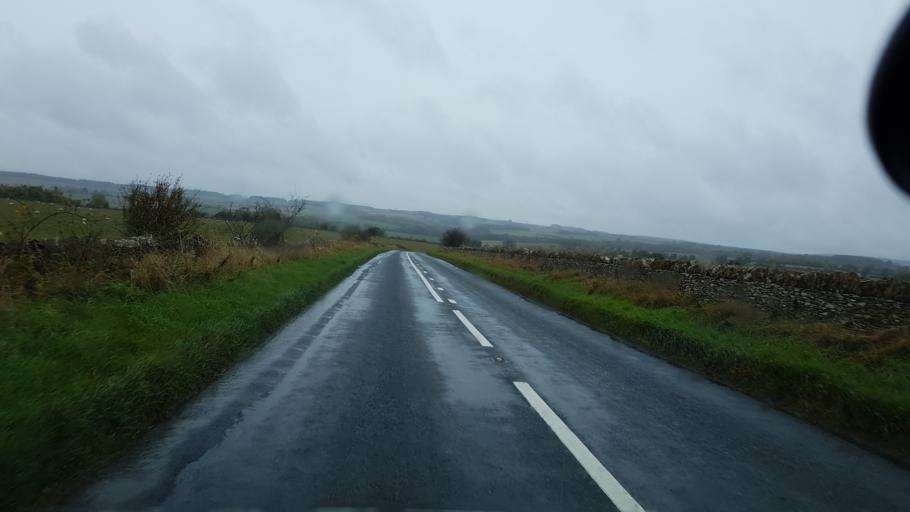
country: GB
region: England
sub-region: Gloucestershire
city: Stow on the Wold
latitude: 51.9449
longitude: -1.7799
